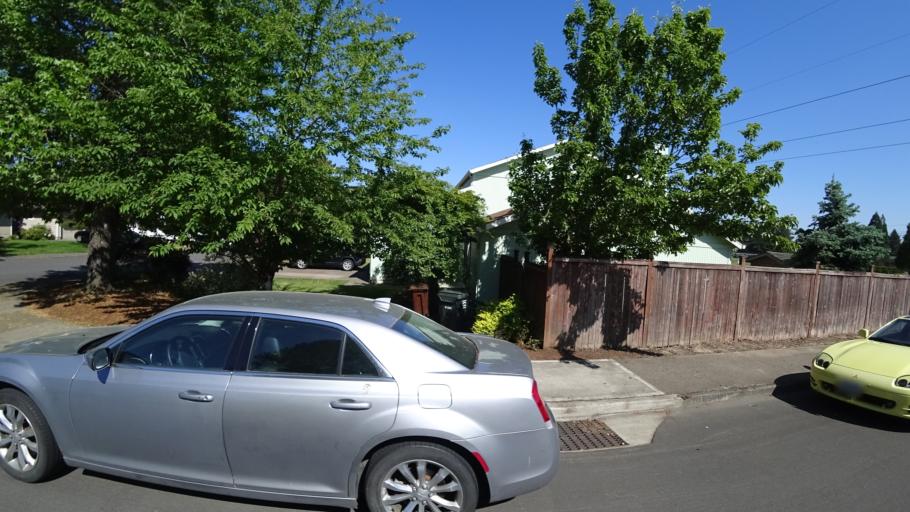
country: US
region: Oregon
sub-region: Washington County
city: Rockcreek
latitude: 45.5578
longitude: -122.8792
